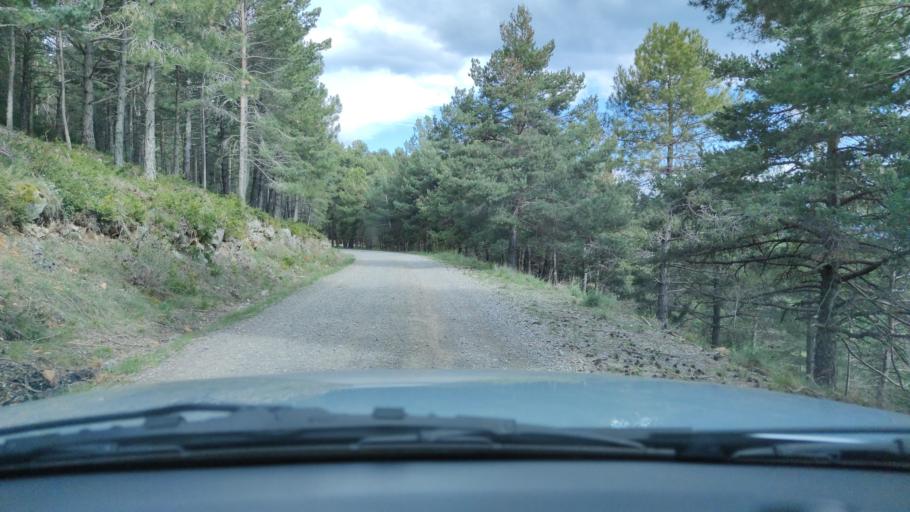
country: ES
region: Catalonia
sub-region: Provincia de Lleida
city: Coll de Nargo
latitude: 42.2475
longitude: 1.4076
